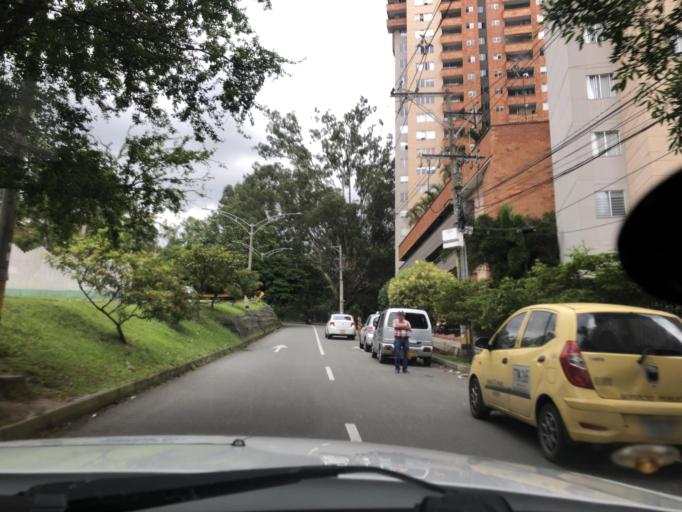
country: CO
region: Antioquia
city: Bello
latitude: 6.3258
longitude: -75.5642
